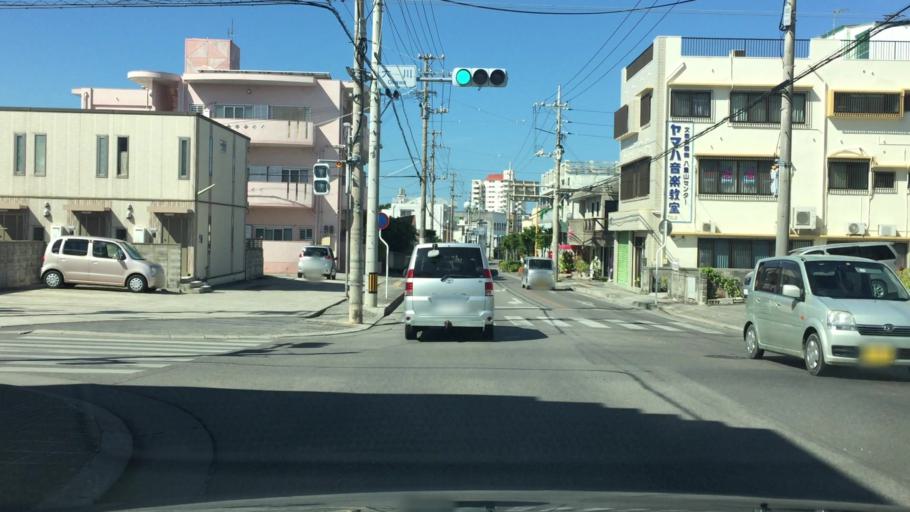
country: JP
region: Okinawa
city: Ishigaki
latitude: 24.3414
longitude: 124.1620
